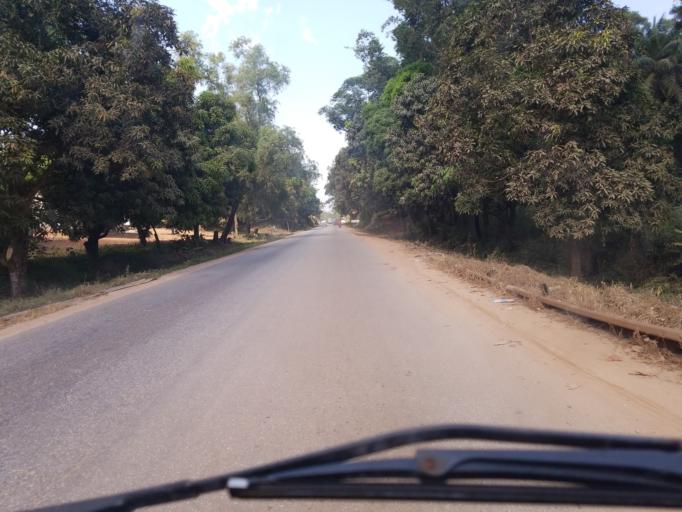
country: GN
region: Kindia
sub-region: Prefecture de Dubreka
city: Dubreka
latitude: 9.8162
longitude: -13.4826
